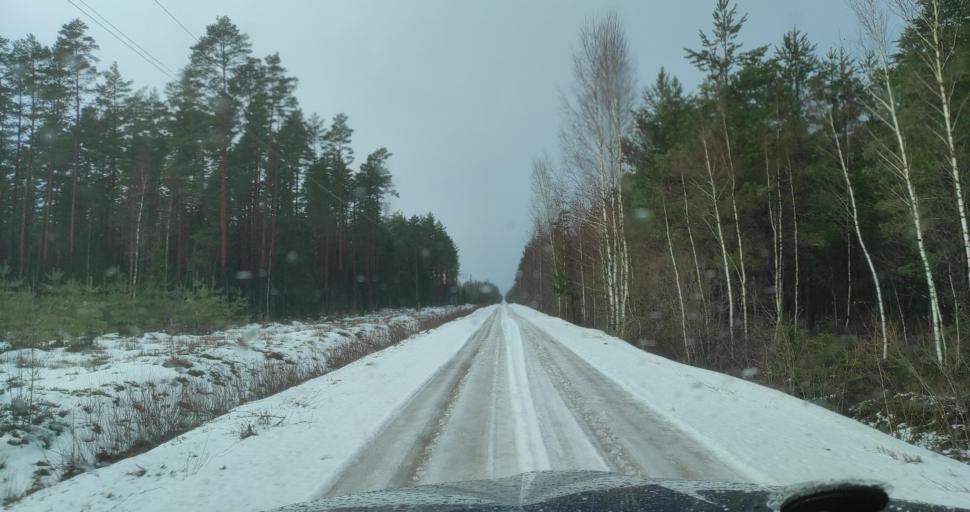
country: LV
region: Dundaga
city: Dundaga
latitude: 57.3847
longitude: 22.1465
